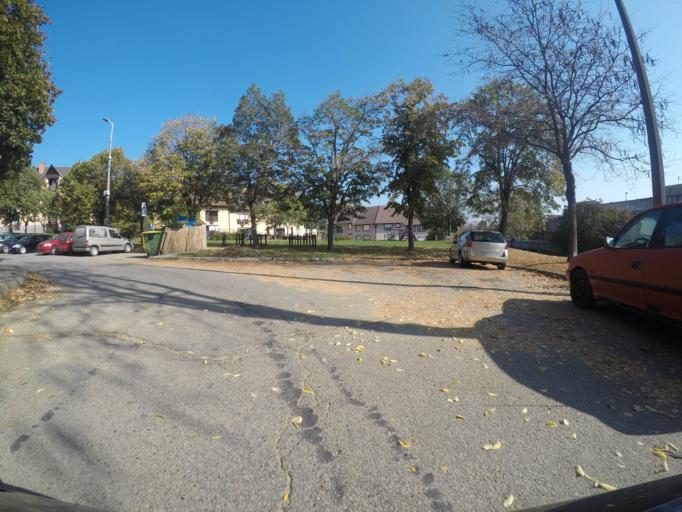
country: HU
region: Baranya
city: Pecs
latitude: 46.0764
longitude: 18.2402
